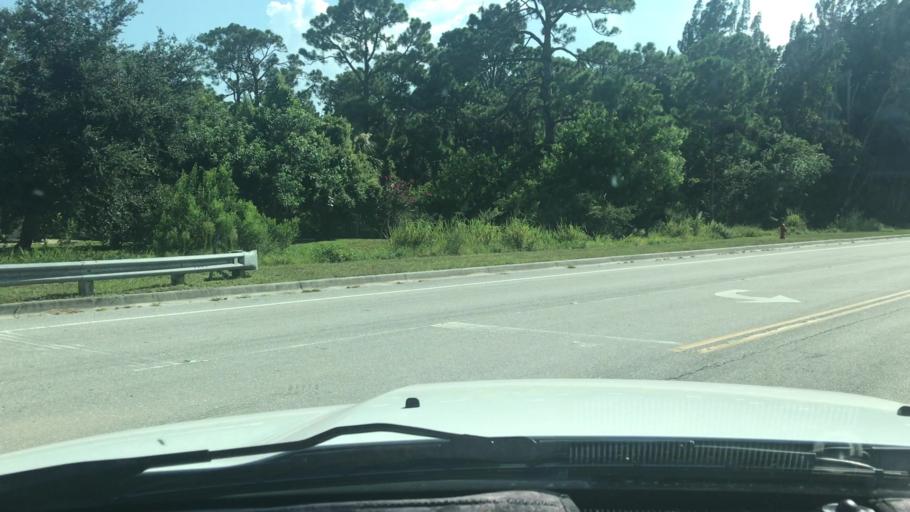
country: US
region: Florida
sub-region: Indian River County
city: Gifford
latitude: 27.6827
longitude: -80.4397
